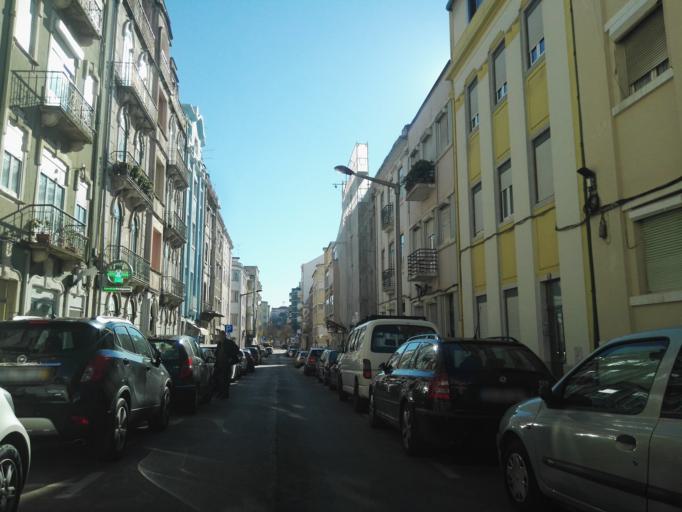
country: PT
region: Lisbon
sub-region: Lisbon
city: Lisbon
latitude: 38.7392
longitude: -9.1311
